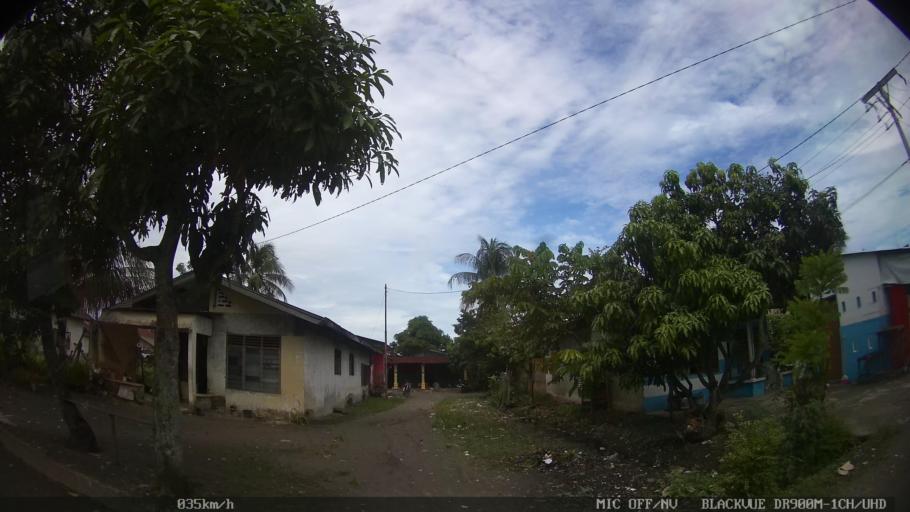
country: ID
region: North Sumatra
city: Sunggal
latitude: 3.5809
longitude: 98.5775
